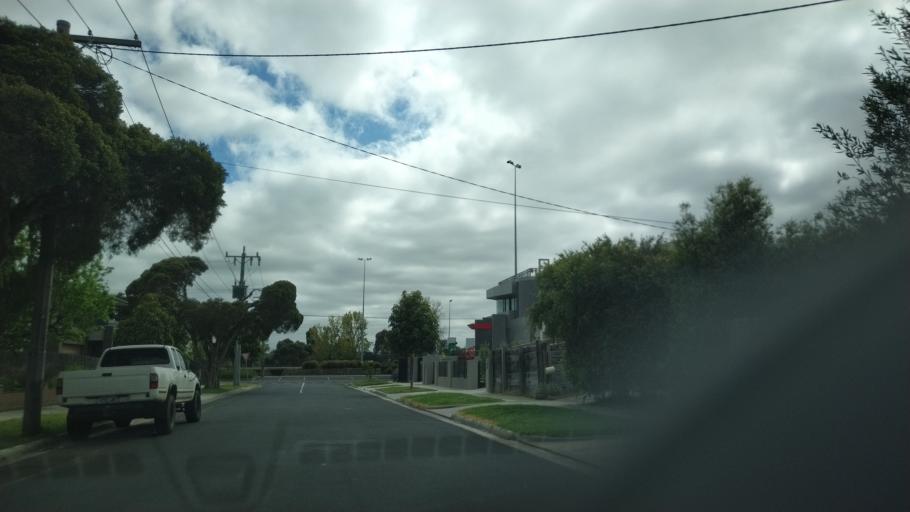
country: AU
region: Victoria
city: Murrumbeena
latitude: -37.9028
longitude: 145.0580
